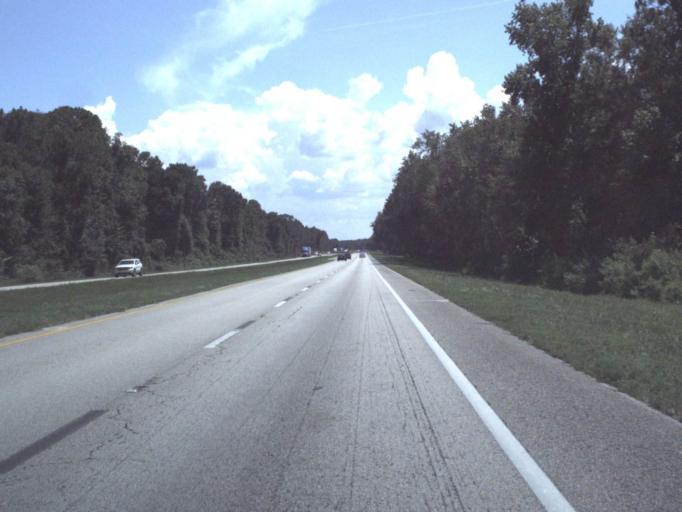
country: US
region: Florida
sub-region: Marion County
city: Citra
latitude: 29.4911
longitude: -82.1008
